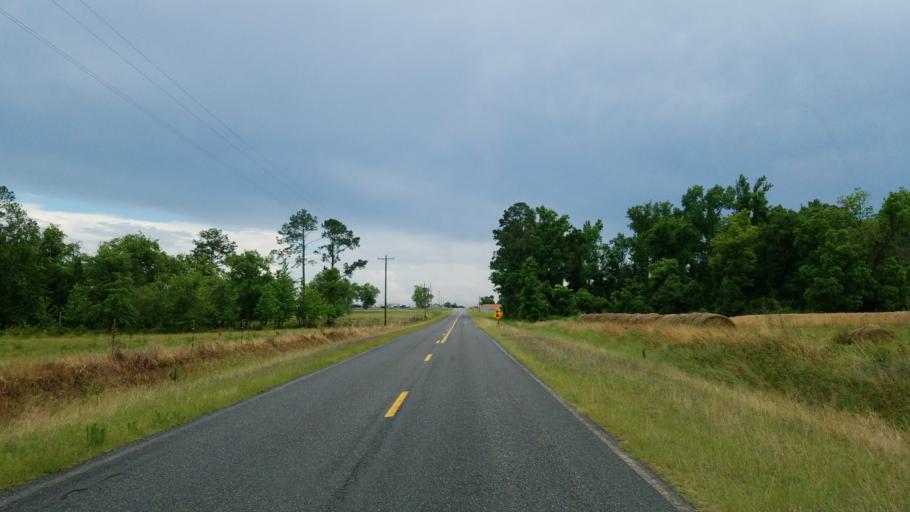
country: US
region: Georgia
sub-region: Dooly County
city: Vienna
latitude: 32.1834
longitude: -83.7979
